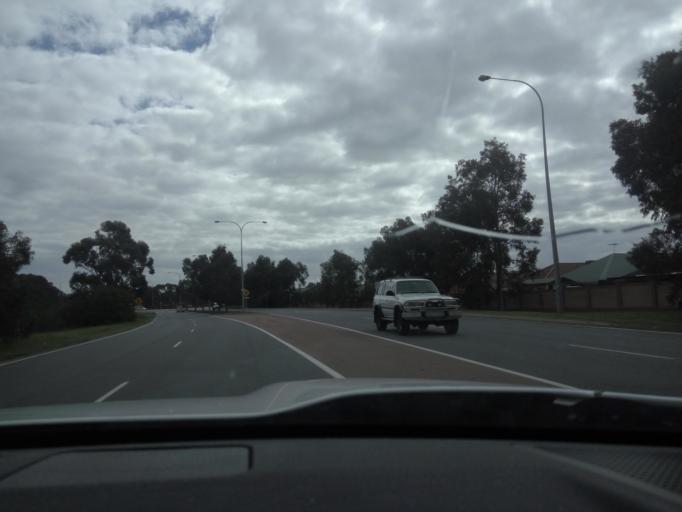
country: AU
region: Western Australia
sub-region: City of Cockburn
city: Bibra Lake
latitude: -32.1042
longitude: 115.8250
